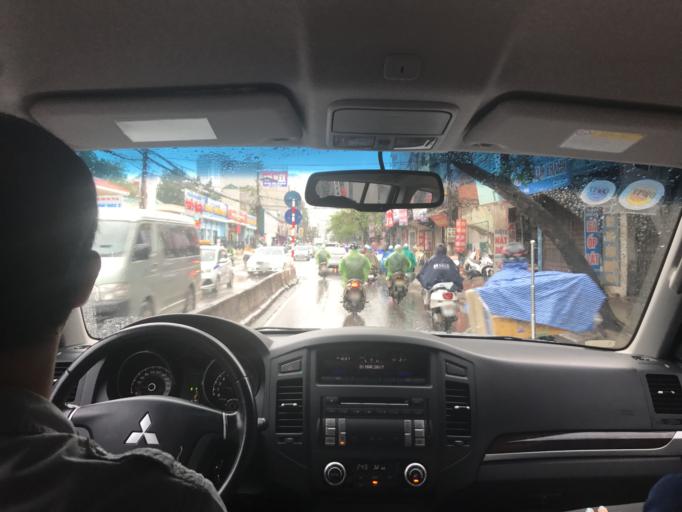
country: VN
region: Ha Noi
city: Dong Da
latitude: 21.0013
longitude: 105.8267
